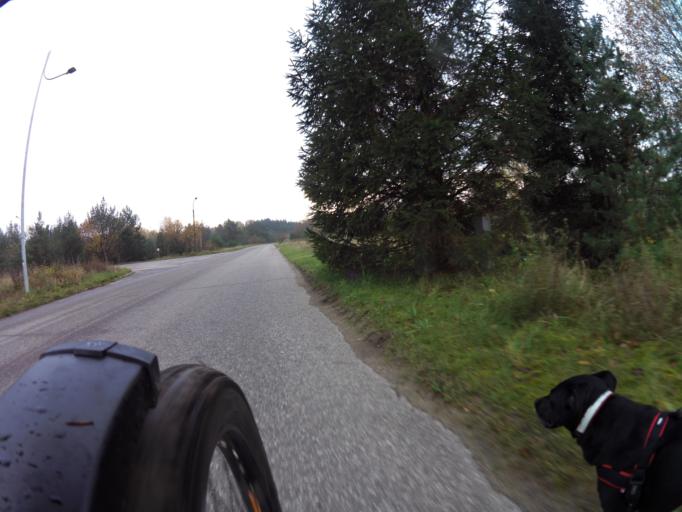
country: PL
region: Pomeranian Voivodeship
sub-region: Powiat wejherowski
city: Gniewino
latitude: 54.7365
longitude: 18.0934
